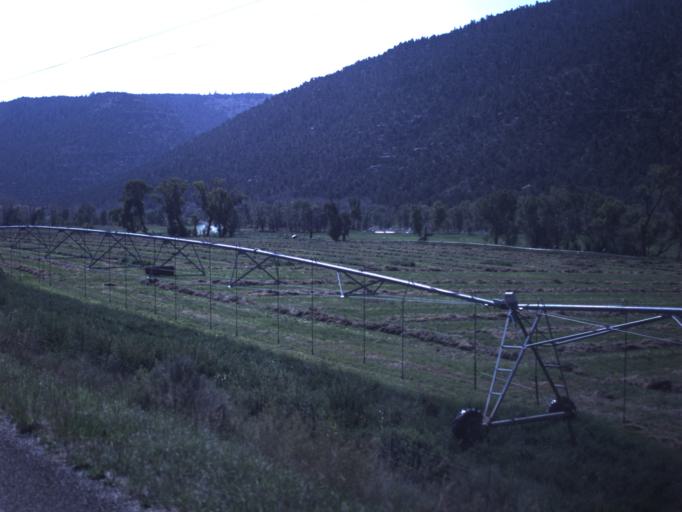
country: US
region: Utah
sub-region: Duchesne County
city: Duchesne
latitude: 40.3025
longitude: -110.6120
